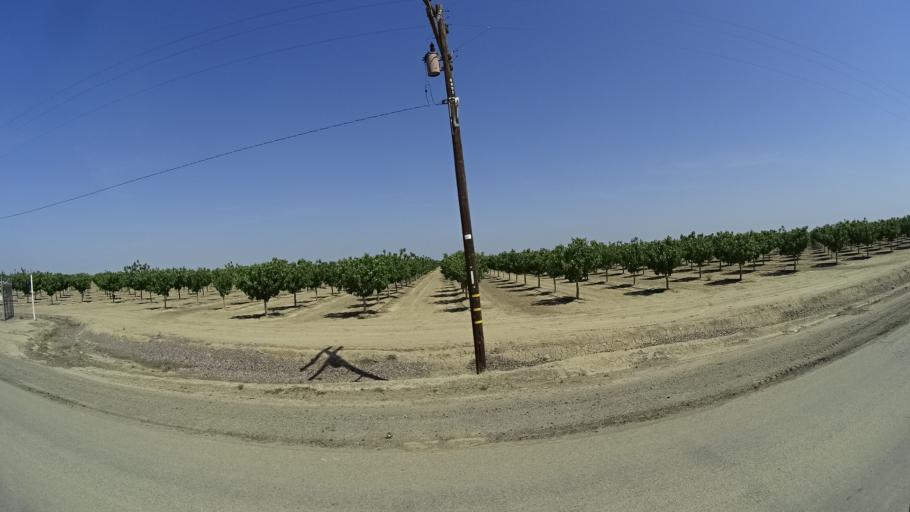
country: US
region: California
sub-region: Fresno County
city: Huron
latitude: 36.1377
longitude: -119.9880
